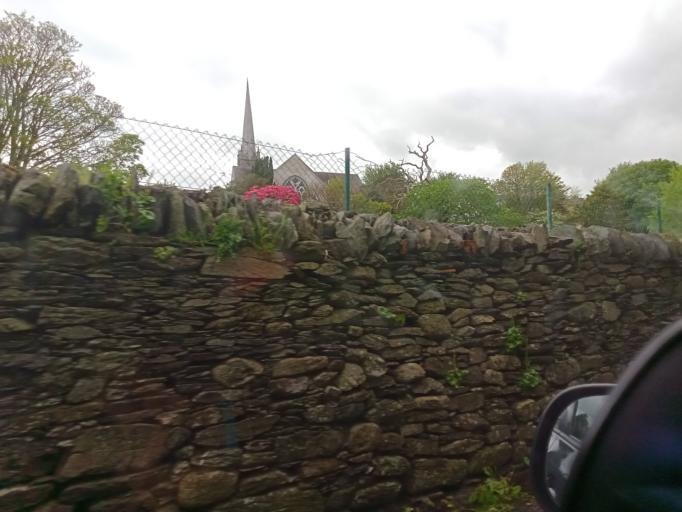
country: IE
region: Munster
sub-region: County Cork
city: Derry
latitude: 51.5781
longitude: -9.0281
